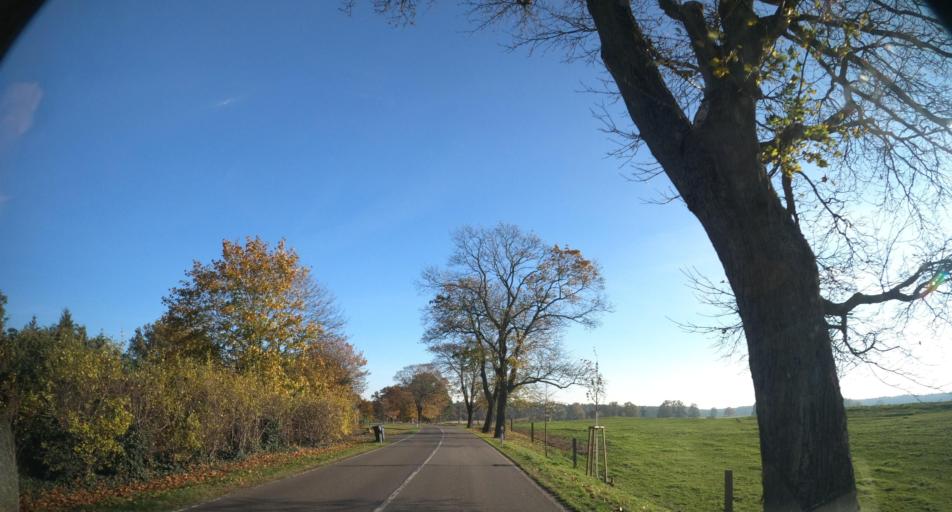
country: DE
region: Mecklenburg-Vorpommern
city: Ahlbeck
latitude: 53.6257
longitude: 14.2706
